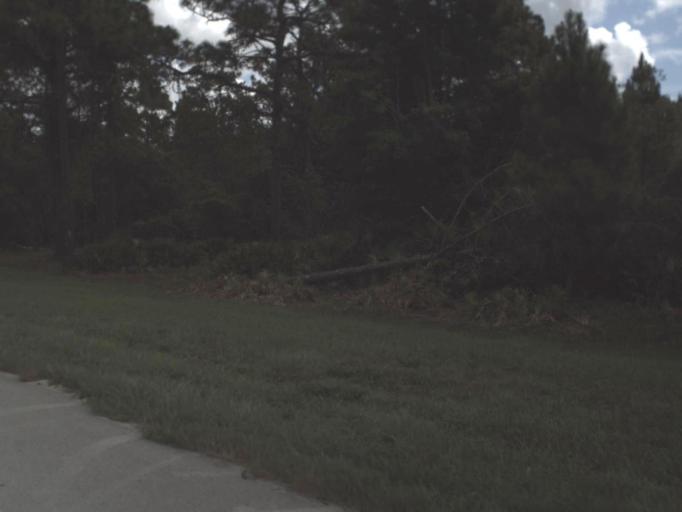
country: US
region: Florida
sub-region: Polk County
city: Polk City
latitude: 28.3443
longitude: -81.8276
